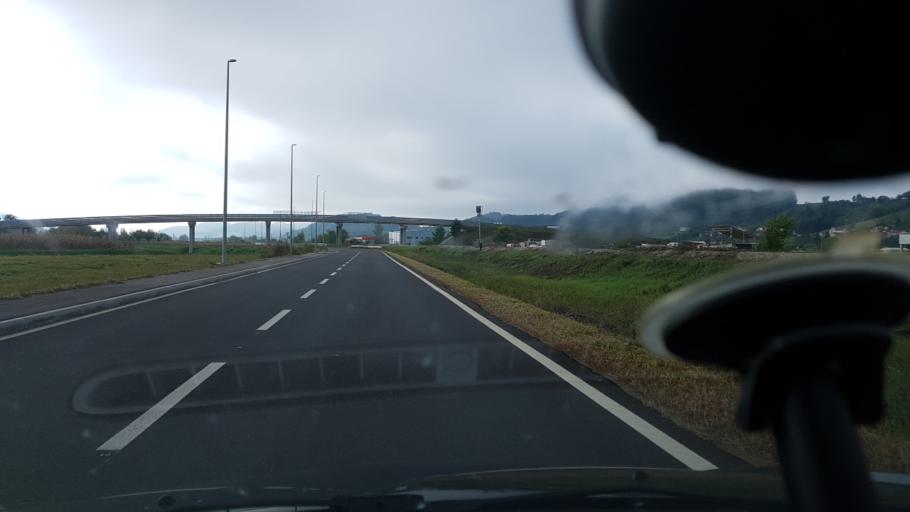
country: HR
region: Krapinsko-Zagorska
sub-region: Grad Krapina
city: Krapina
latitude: 46.1494
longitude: 15.8742
